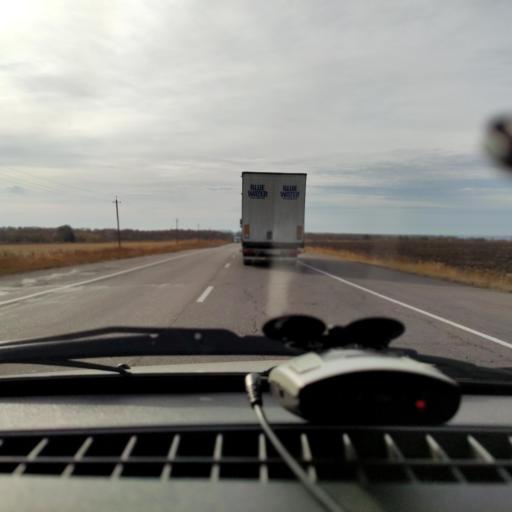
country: RU
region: Voronezj
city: Strelitsa
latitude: 51.5271
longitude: 38.9688
